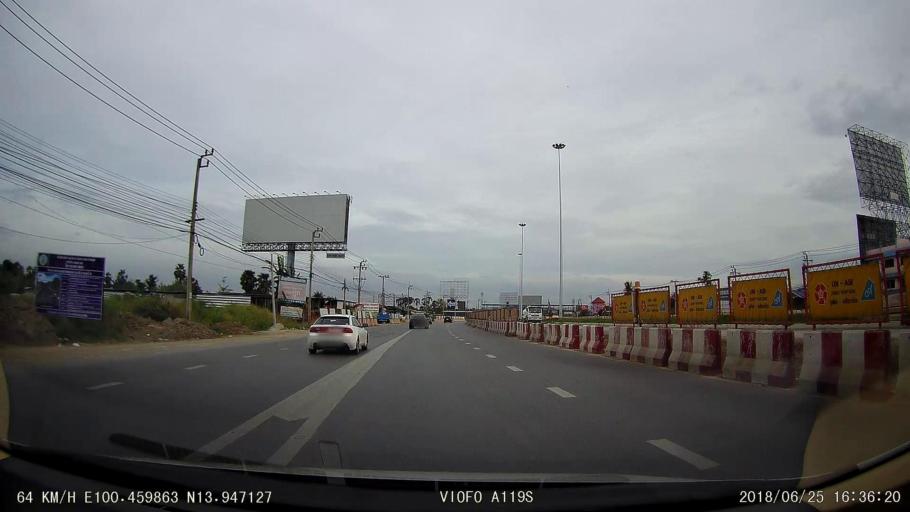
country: TH
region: Nonthaburi
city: Bang Bua Thong
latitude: 13.9469
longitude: 100.4600
